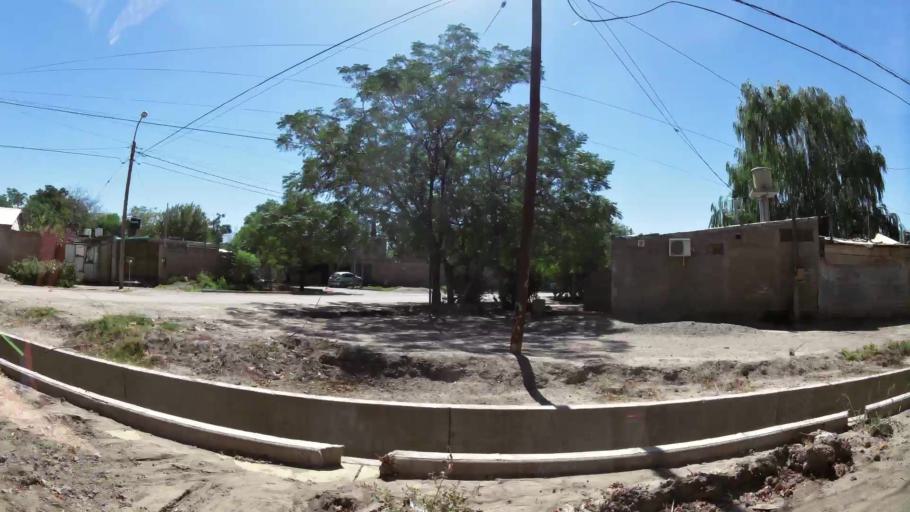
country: AR
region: Mendoza
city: Mendoza
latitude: -32.8779
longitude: -68.8102
